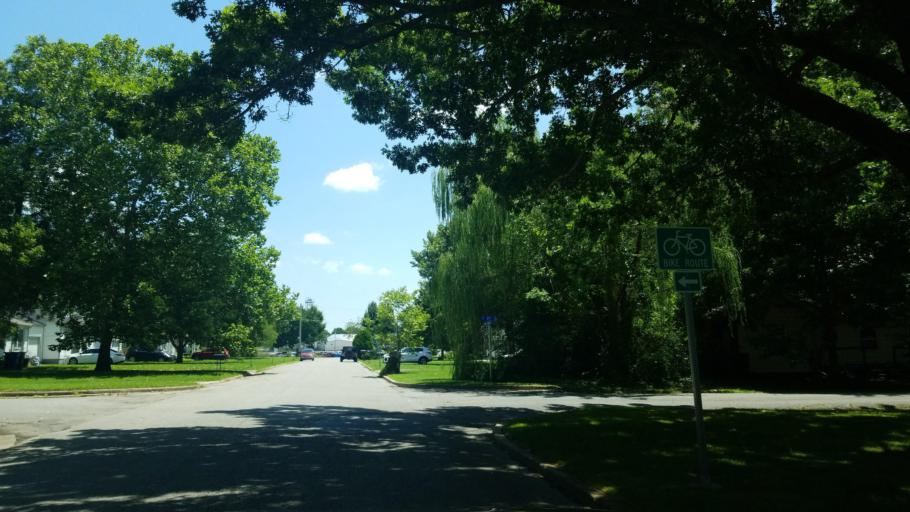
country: US
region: Oklahoma
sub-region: Tulsa County
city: Broken Arrow
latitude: 36.0514
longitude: -95.7856
